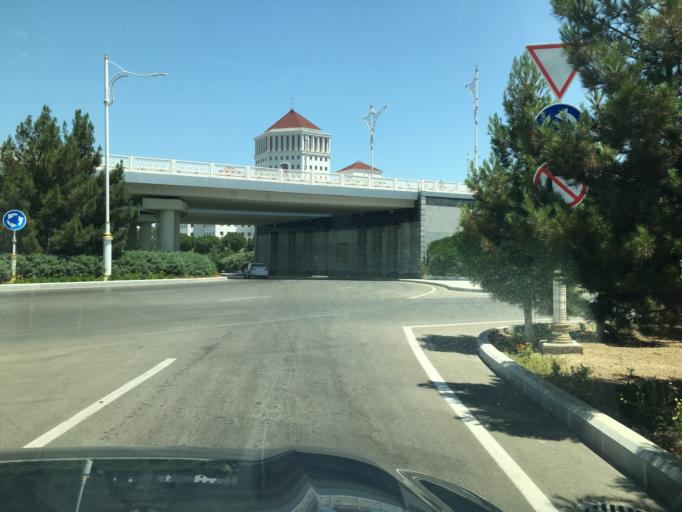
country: TM
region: Ahal
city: Ashgabat
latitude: 37.8783
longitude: 58.3873
